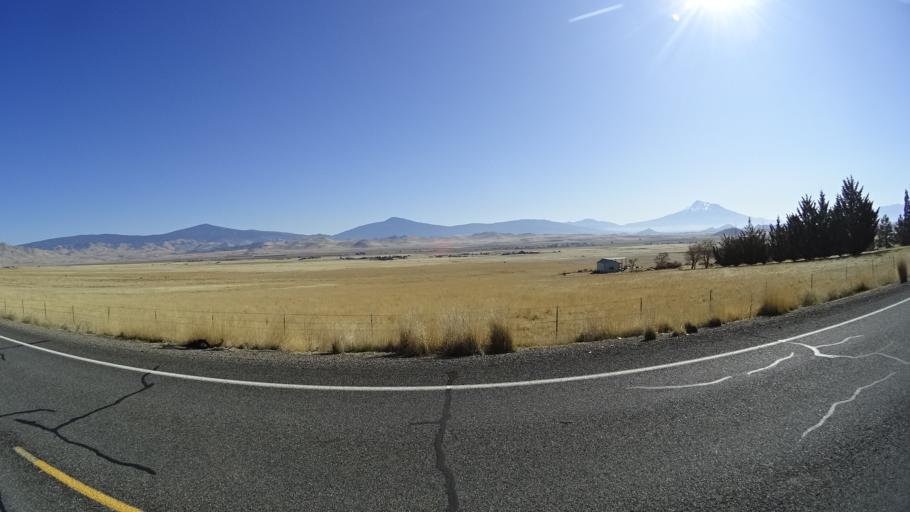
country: US
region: California
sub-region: Siskiyou County
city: Montague
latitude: 41.7891
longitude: -122.5157
